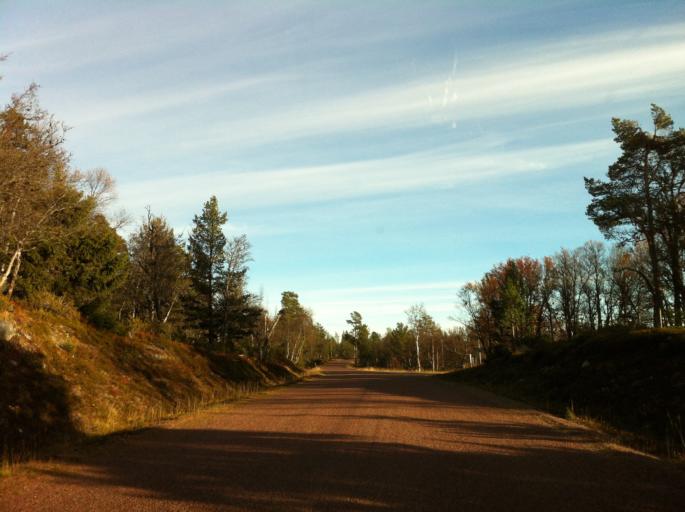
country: NO
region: Hedmark
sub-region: Engerdal
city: Engerdal
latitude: 62.0828
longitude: 12.1269
